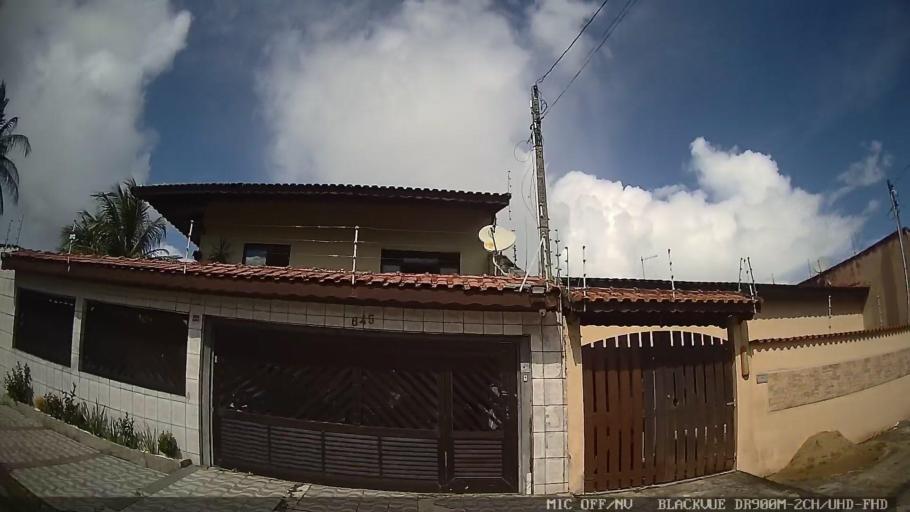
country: BR
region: Sao Paulo
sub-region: Itanhaem
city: Itanhaem
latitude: -24.2422
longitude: -46.8955
